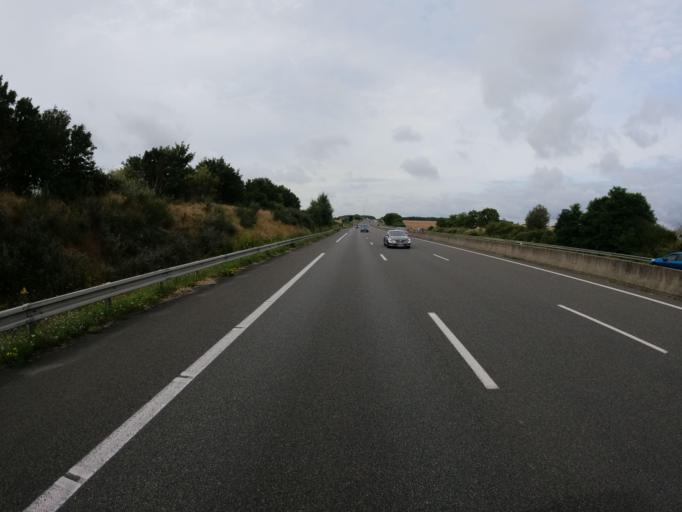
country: FR
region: Centre
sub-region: Departement d'Indre-et-Loire
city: Cangey
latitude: 47.5633
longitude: 1.0363
